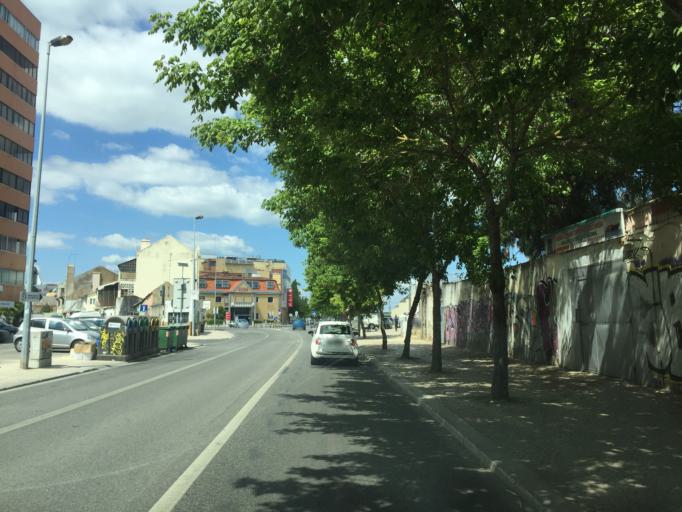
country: PT
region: Setubal
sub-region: Almada
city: Almada
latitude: 38.6723
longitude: -9.1556
